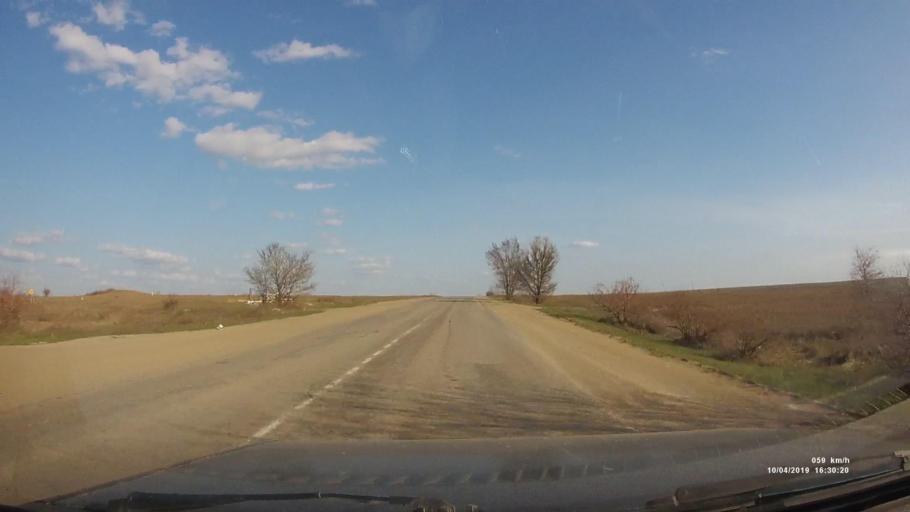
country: RU
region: Rostov
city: Staraya Stanitsa
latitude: 48.2627
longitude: 40.3643
